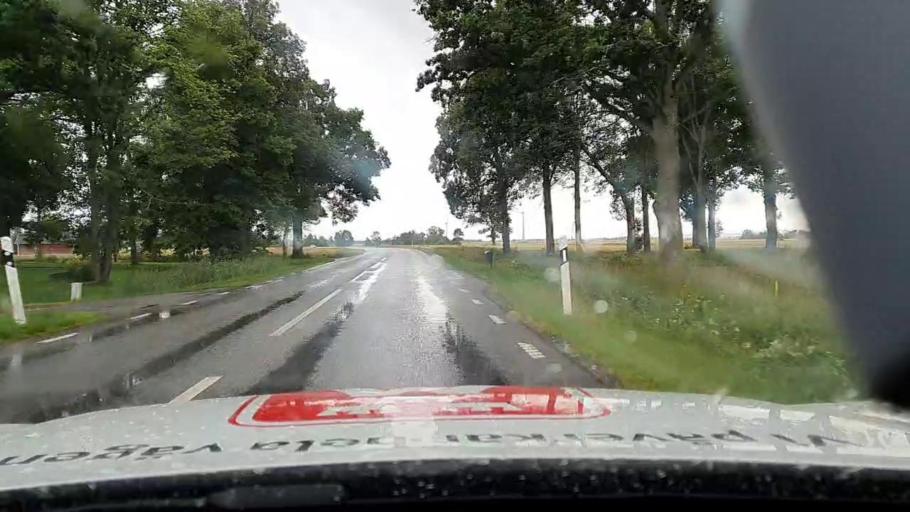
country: SE
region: Vaestra Goetaland
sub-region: Toreboda Kommun
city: Toereboda
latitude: 58.6179
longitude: 14.0123
